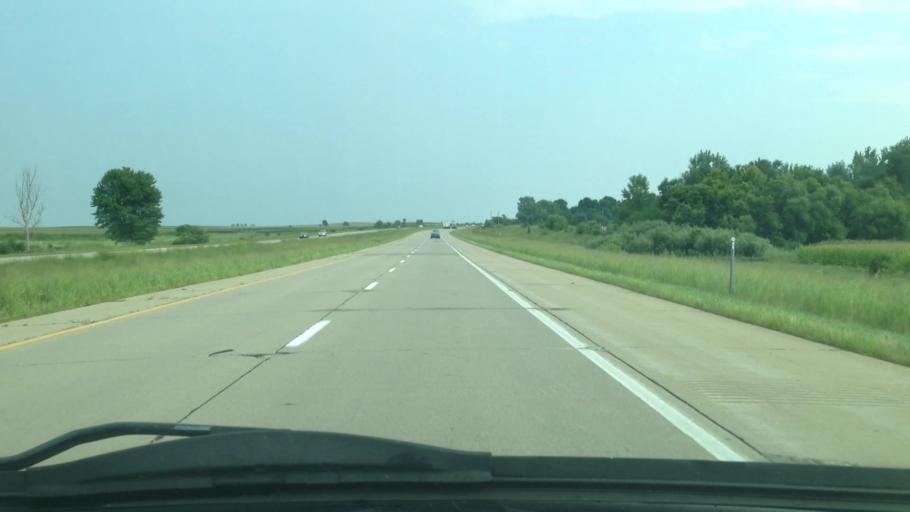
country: US
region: Iowa
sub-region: Benton County
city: Urbana
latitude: 42.2785
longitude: -91.9356
